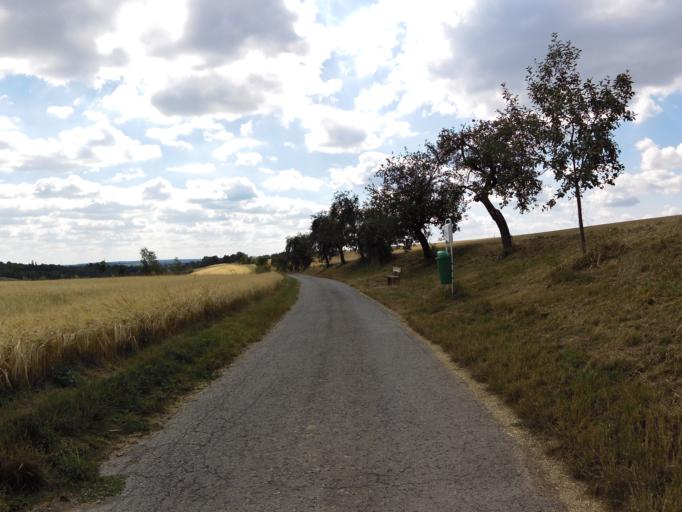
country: DE
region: Bavaria
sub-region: Regierungsbezirk Unterfranken
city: Gerbrunn
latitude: 49.7793
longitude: 10.0142
